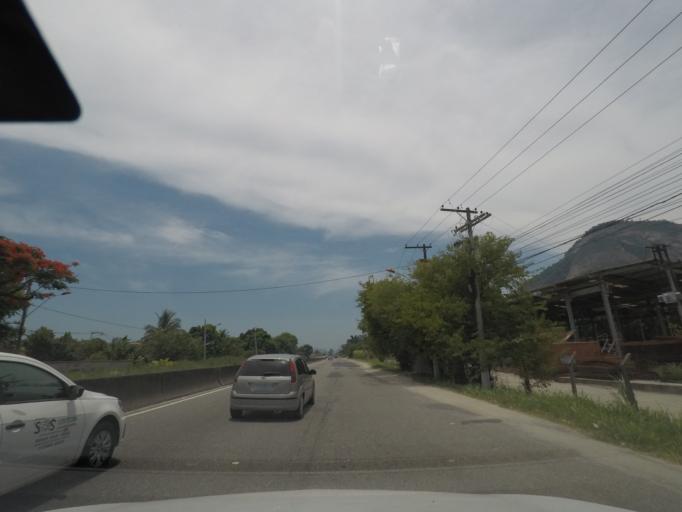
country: BR
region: Rio de Janeiro
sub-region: Marica
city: Marica
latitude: -22.9340
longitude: -42.8966
